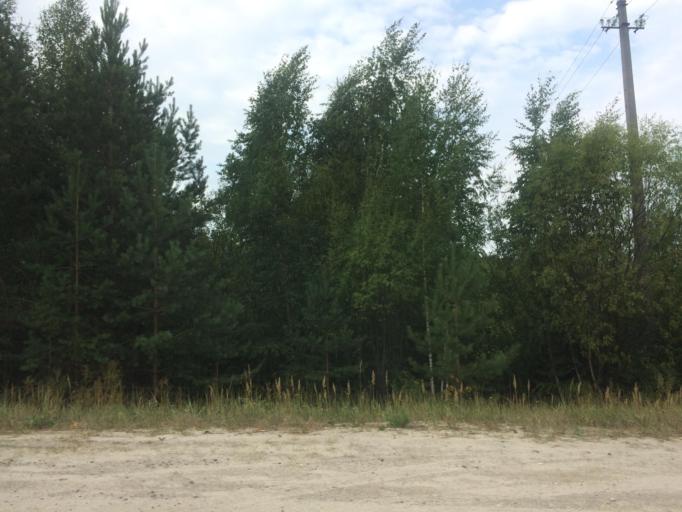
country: RU
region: Mariy-El
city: Yoshkar-Ola
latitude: 56.5427
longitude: 47.9817
